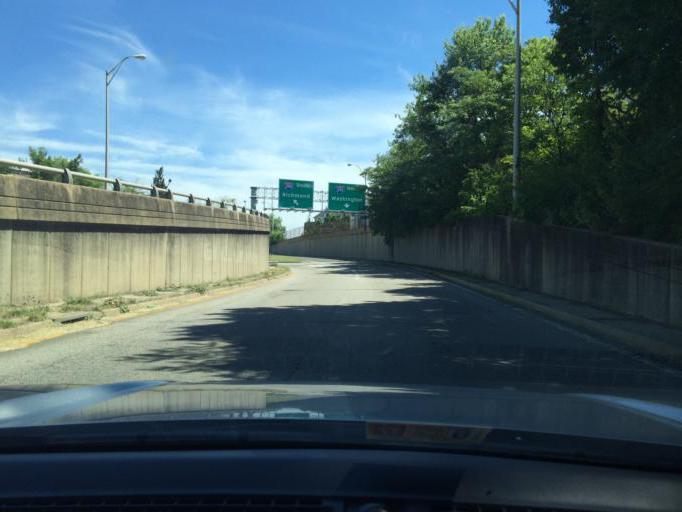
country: US
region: Virginia
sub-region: Arlington County
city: Arlington
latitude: 38.8464
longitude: -77.0783
